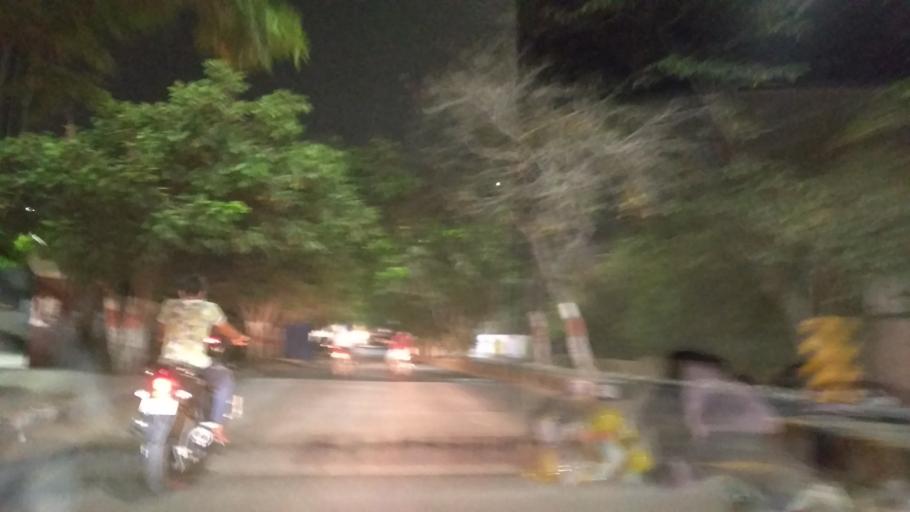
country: IN
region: Telangana
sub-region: Rangareddi
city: Kukatpalli
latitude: 17.4433
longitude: 78.4369
